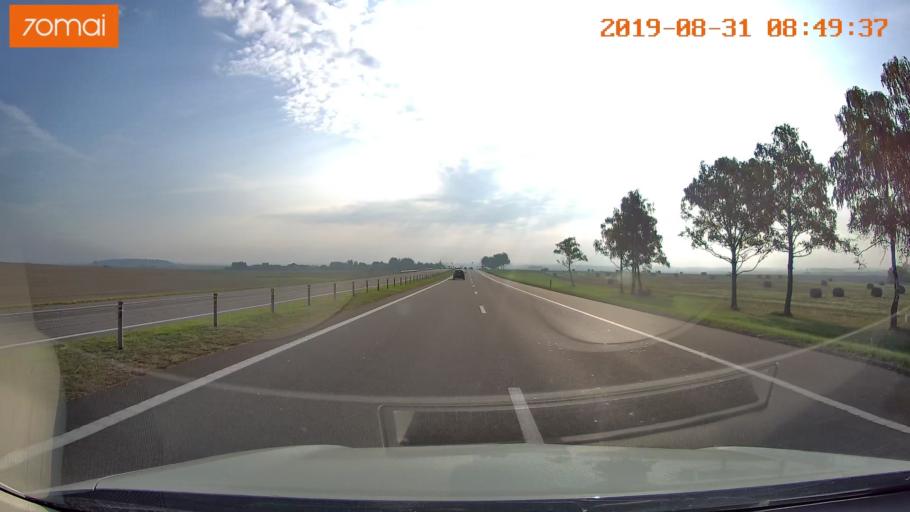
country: BY
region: Minsk
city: Zamostochcha
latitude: 53.7615
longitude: 27.9235
